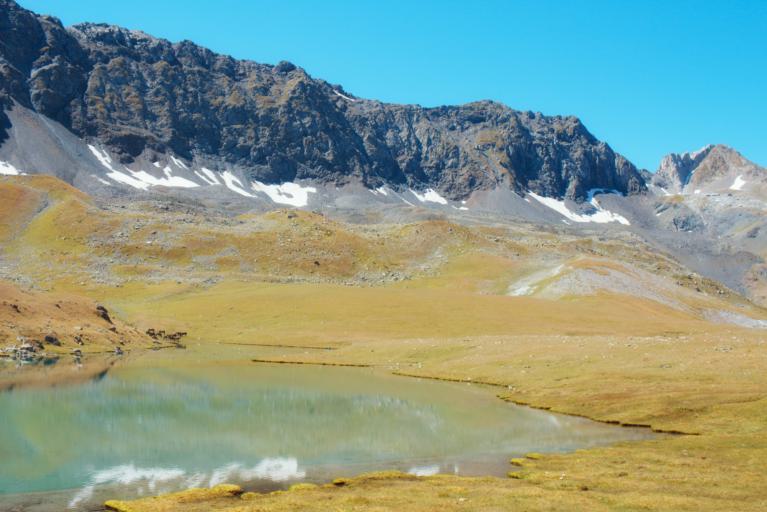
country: RU
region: Karachayevo-Cherkesiya
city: Nizhniy Arkhyz
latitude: 43.6053
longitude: 41.1618
